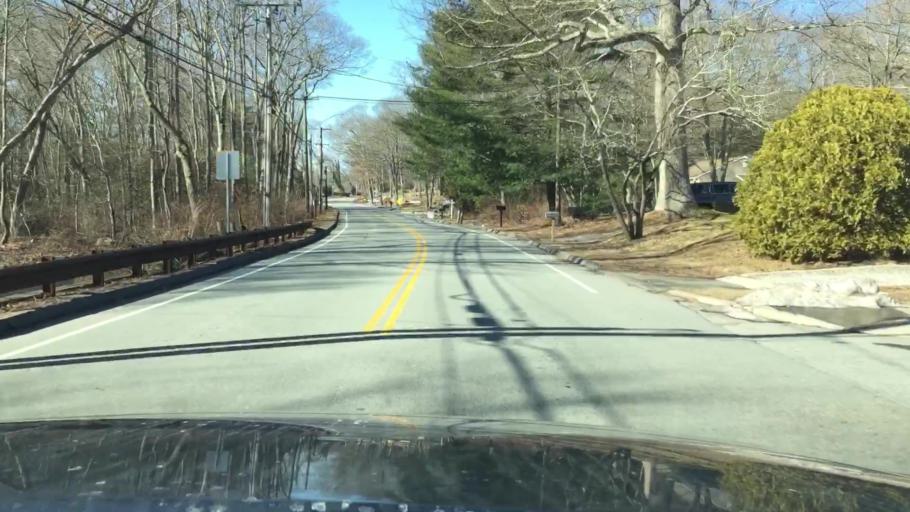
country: US
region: Connecticut
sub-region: New London County
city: Conning Towers-Nautilus Park
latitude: 41.3735
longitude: -72.0543
